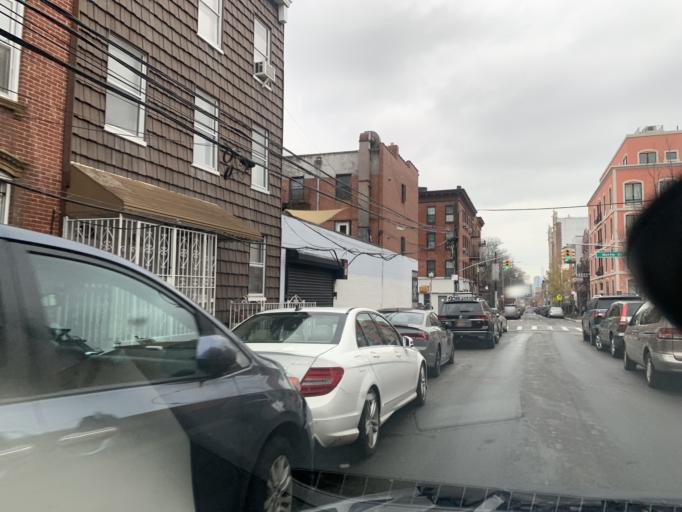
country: US
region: New York
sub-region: Kings County
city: Brooklyn
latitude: 40.6937
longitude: -73.9601
